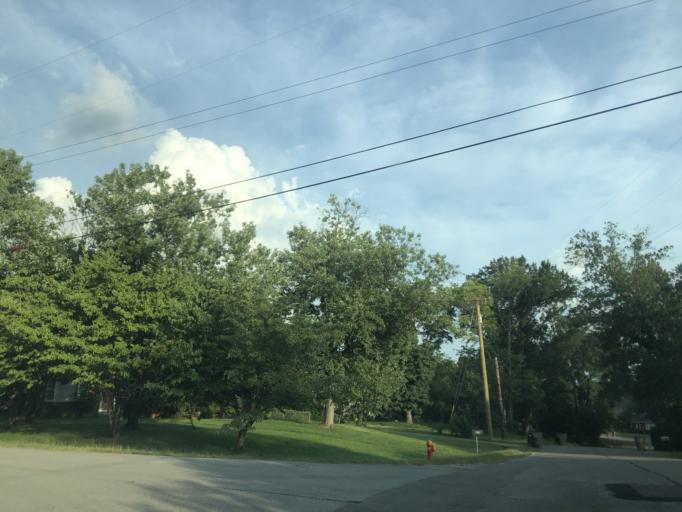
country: US
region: Tennessee
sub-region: Davidson County
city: Nashville
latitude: 36.1545
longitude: -86.6993
